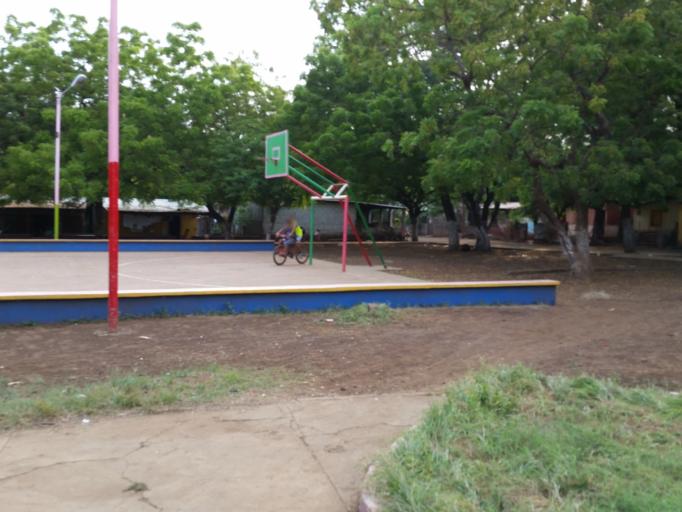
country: NI
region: Managua
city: Masachapa
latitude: 11.7881
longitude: -86.5148
